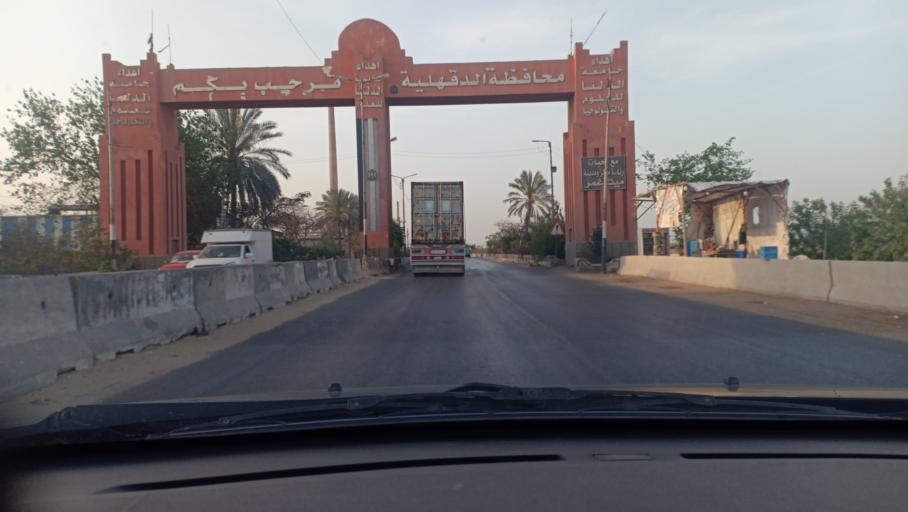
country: EG
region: Muhafazat al Gharbiyah
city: Zifta
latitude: 30.6037
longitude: 31.2748
